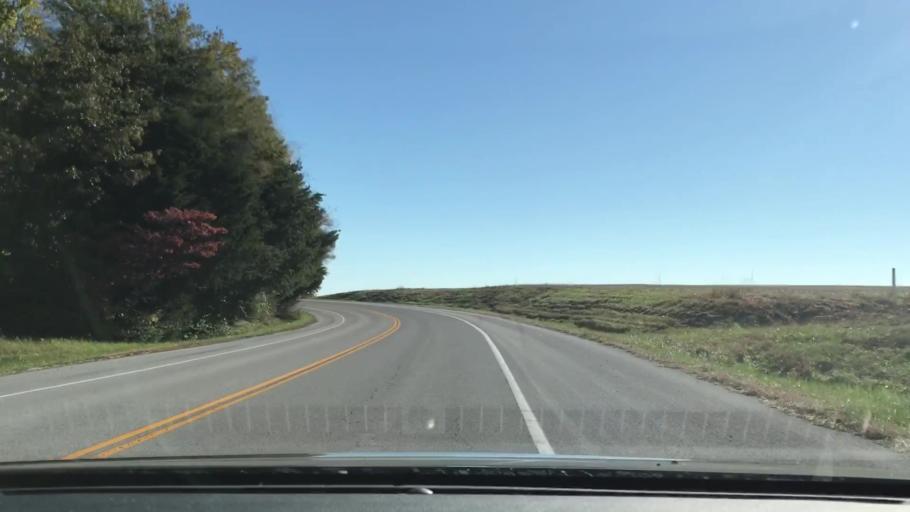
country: US
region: Kentucky
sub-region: Logan County
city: Auburn
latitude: 36.8656
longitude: -86.6964
